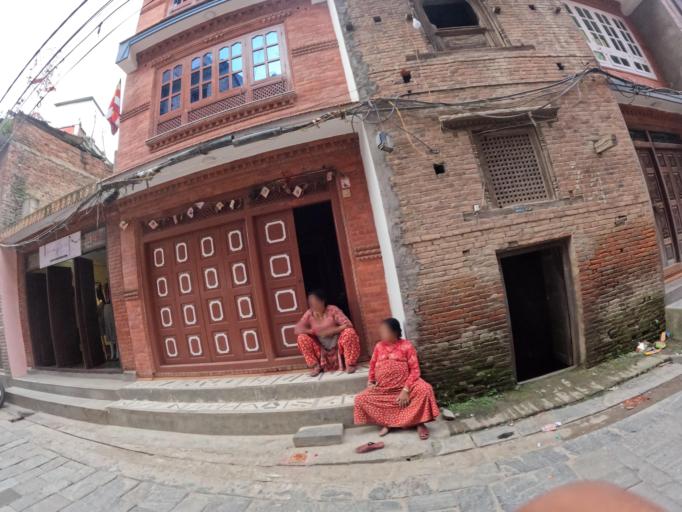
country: NP
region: Central Region
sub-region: Bagmati Zone
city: Bhaktapur
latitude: 27.6823
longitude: 85.3869
